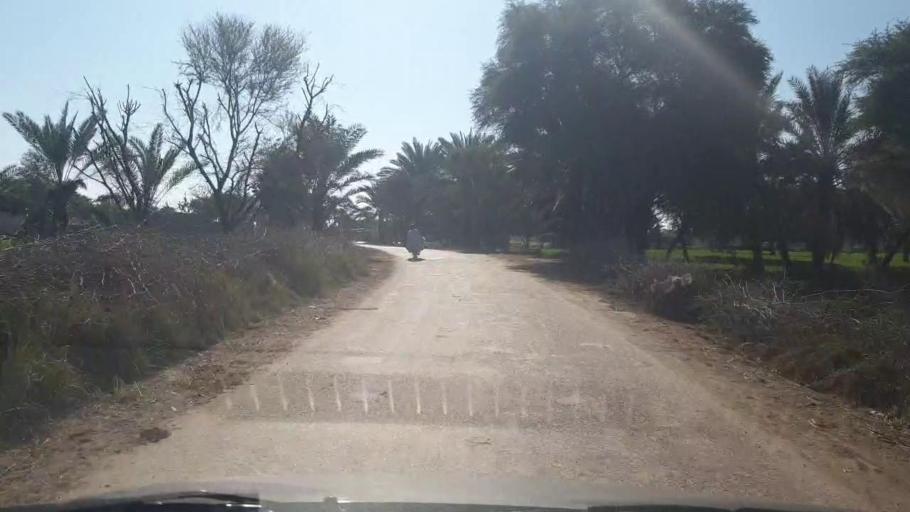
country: PK
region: Sindh
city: Bozdar
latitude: 27.1539
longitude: 68.6546
